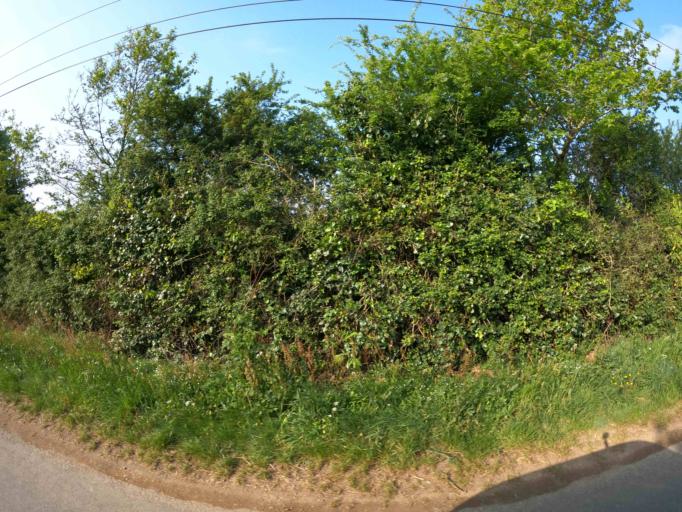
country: FR
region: Pays de la Loire
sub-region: Departement de Maine-et-Loire
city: Saint-Andre-de-la-Marche
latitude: 47.0735
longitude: -0.9913
